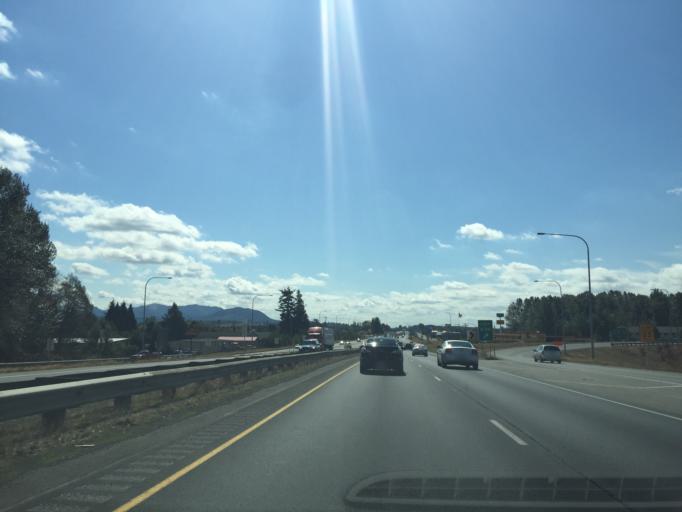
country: US
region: Washington
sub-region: Skagit County
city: Burlington
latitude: 48.4696
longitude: -122.3420
